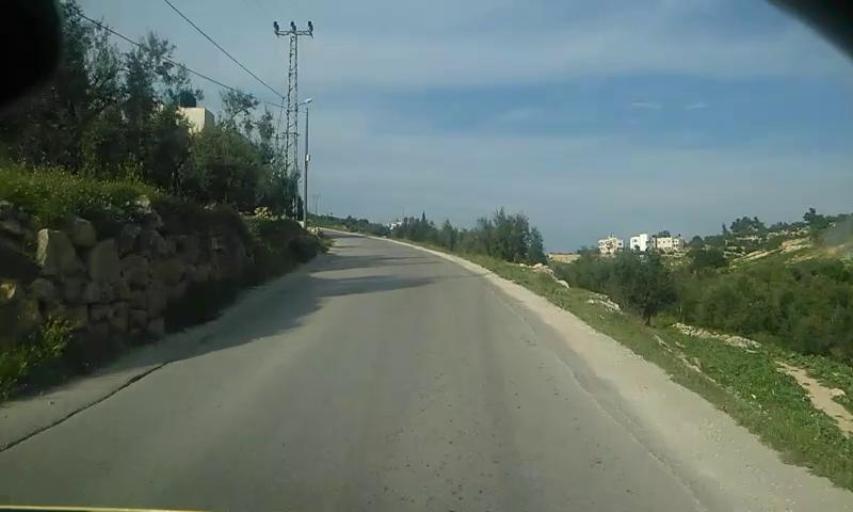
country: PS
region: West Bank
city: Bayt Ula
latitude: 31.5847
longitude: 35.0233
